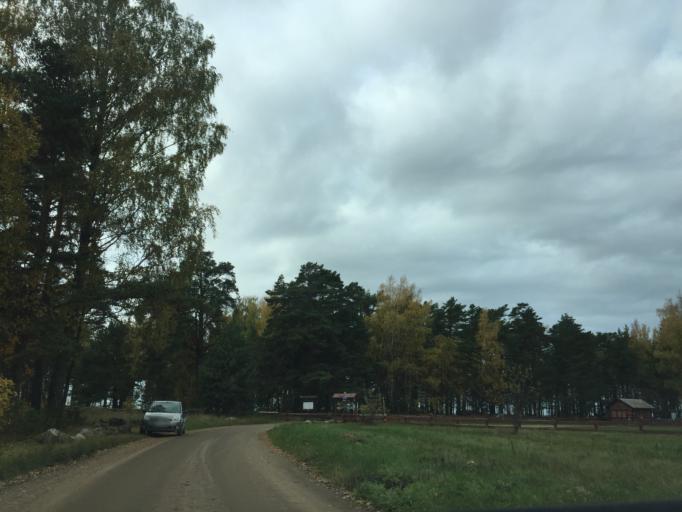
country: LV
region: Salacgrivas
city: Salacgriva
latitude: 57.5784
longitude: 24.3672
